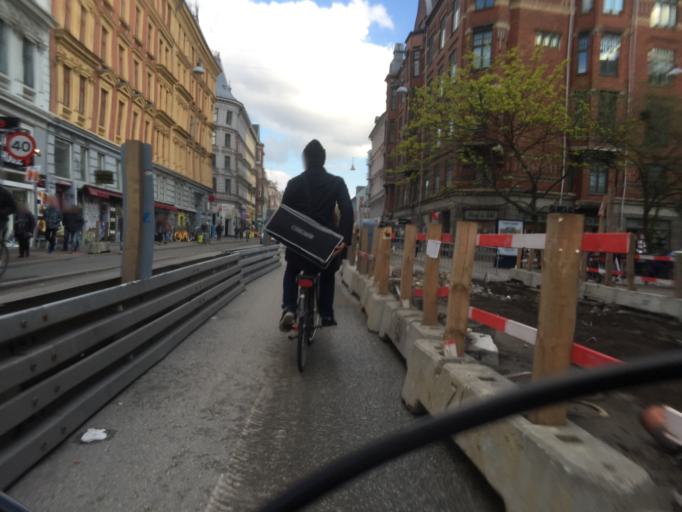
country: DK
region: Capital Region
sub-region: Frederiksberg Kommune
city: Frederiksberg
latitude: 55.6955
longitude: 12.5470
